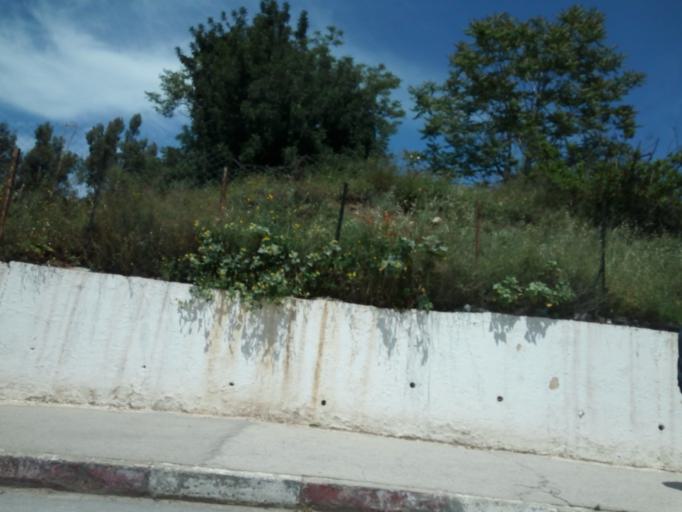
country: DZ
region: Constantine
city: Constantine
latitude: 36.3725
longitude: 6.6202
